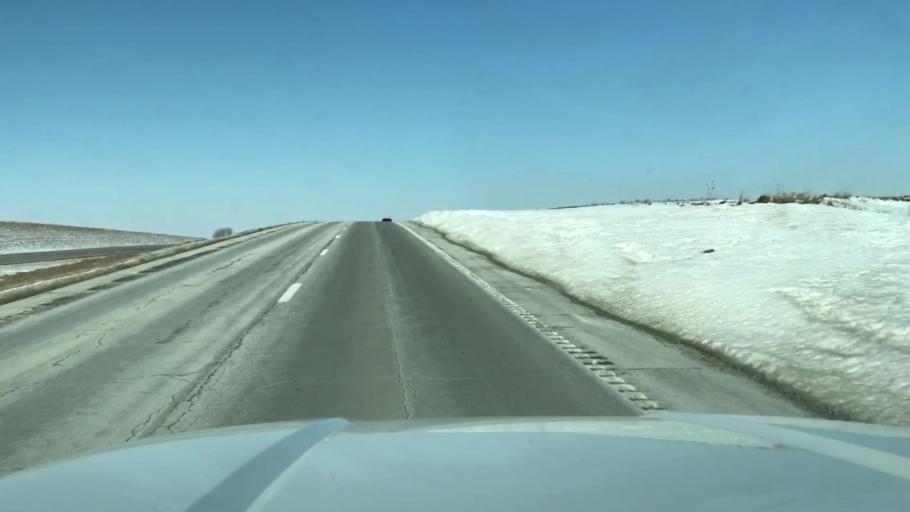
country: US
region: Missouri
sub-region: Andrew County
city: Savannah
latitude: 39.9720
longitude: -94.8729
